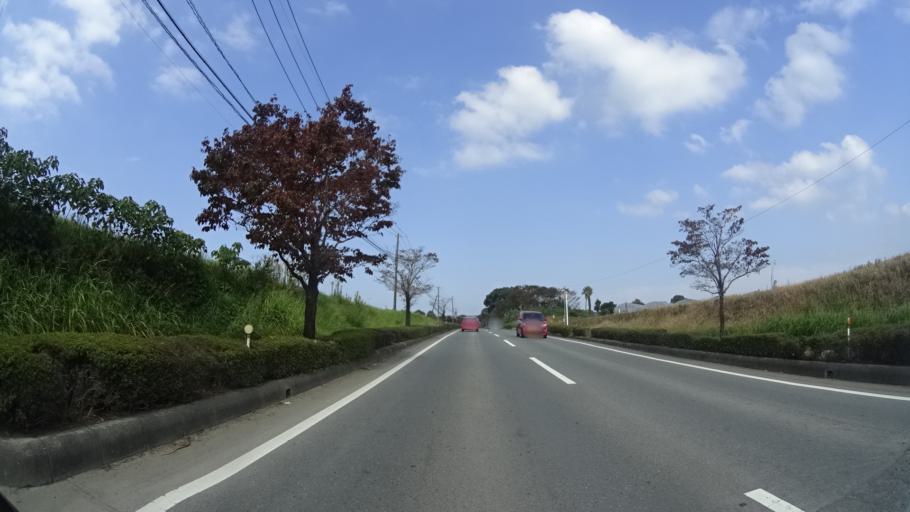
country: JP
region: Kumamoto
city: Ozu
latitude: 32.8059
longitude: 130.8247
